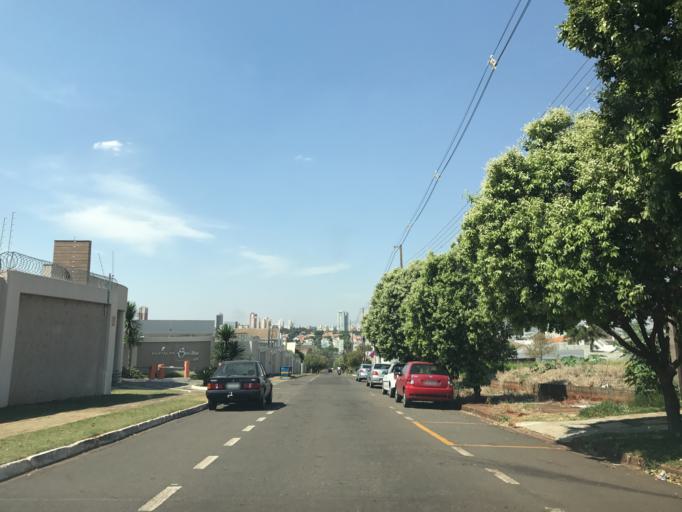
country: BR
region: Parana
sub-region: Maringa
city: Maringa
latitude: -23.4450
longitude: -51.9496
